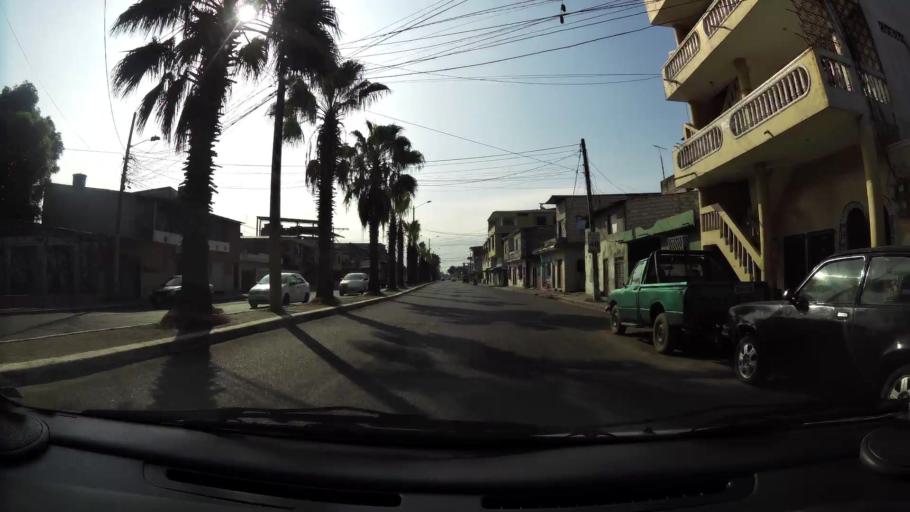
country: EC
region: Guayas
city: Eloy Alfaro
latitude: -2.1704
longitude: -79.8471
